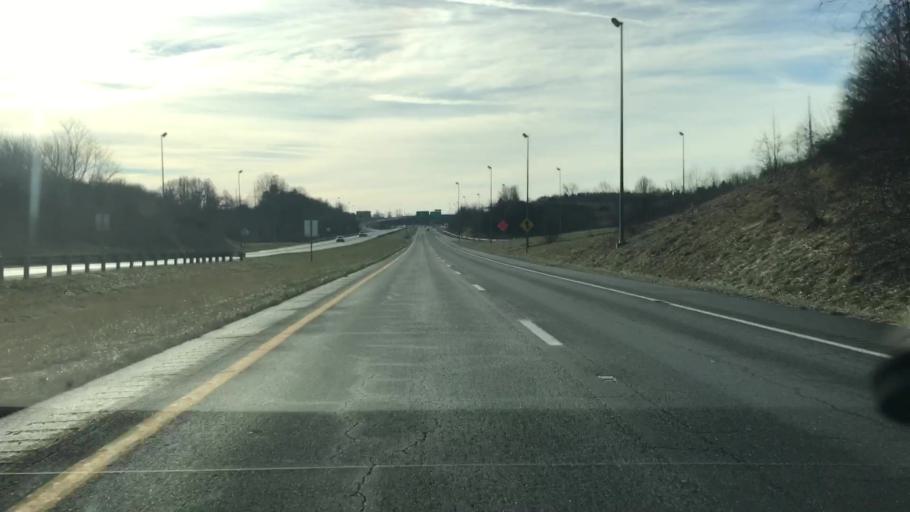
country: US
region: Virginia
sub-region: Montgomery County
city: Merrimac
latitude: 37.1639
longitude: -80.4145
